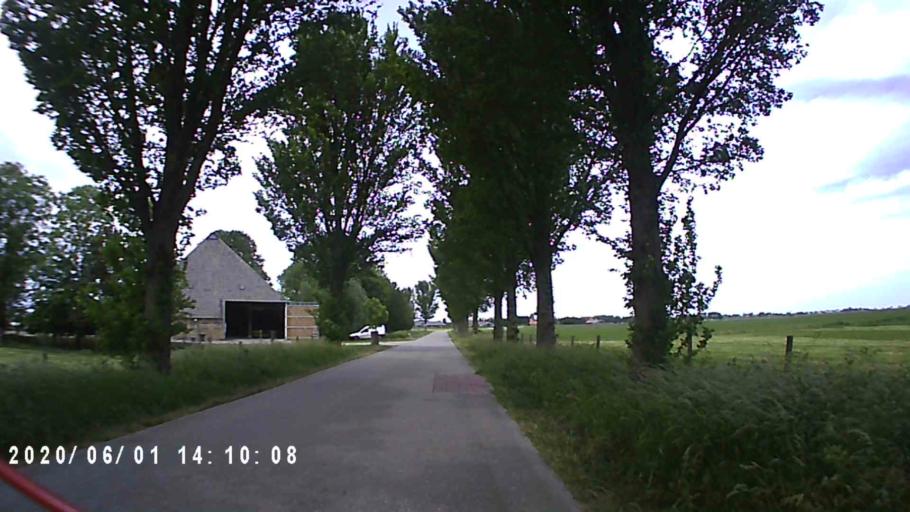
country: NL
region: Friesland
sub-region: Gemeente Littenseradiel
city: Winsum
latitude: 53.1223
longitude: 5.6484
